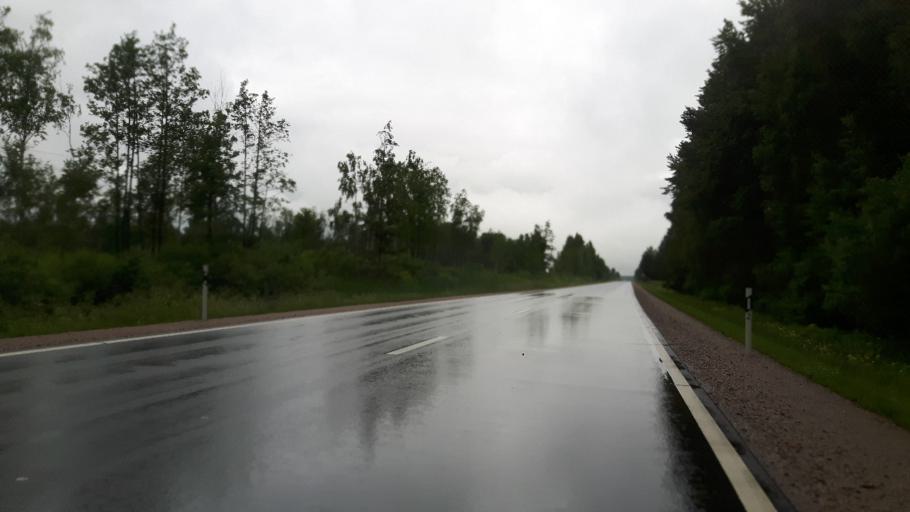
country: LV
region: Nica
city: Nica
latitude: 56.2814
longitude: 21.0901
